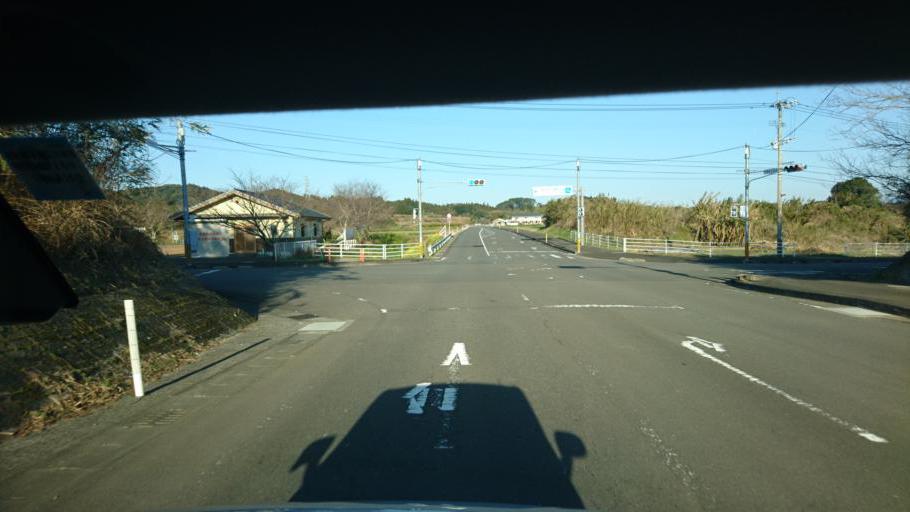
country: JP
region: Miyazaki
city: Miyazaki-shi
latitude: 31.8510
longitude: 131.3780
